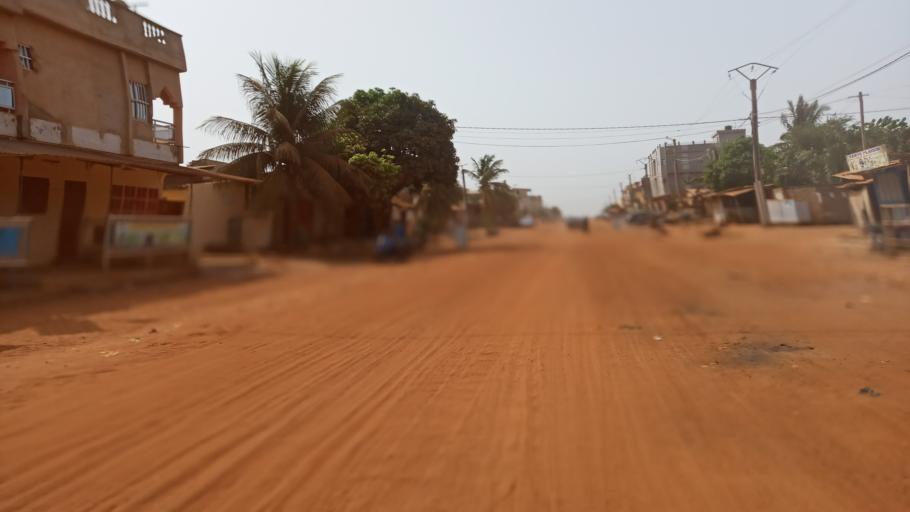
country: TG
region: Maritime
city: Lome
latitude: 6.2003
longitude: 1.1696
